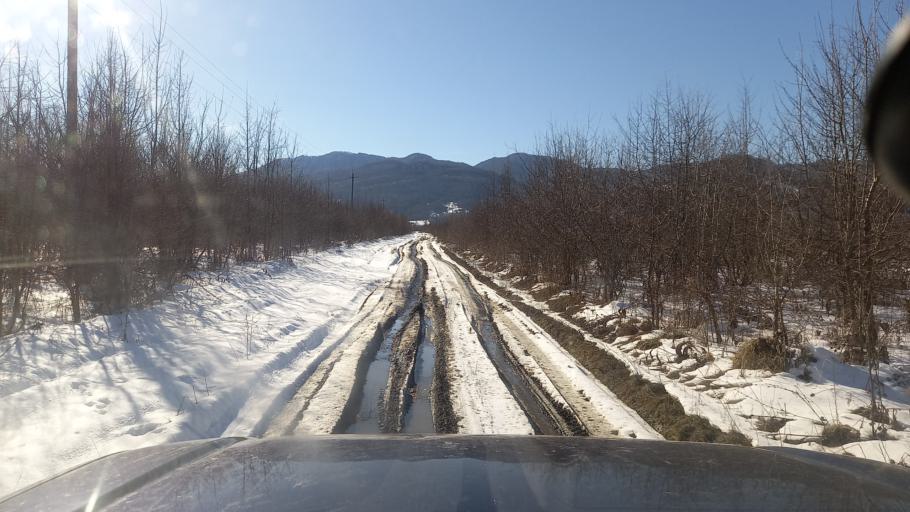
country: RU
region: Adygeya
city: Kamennomostskiy
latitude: 44.2133
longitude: 40.1694
